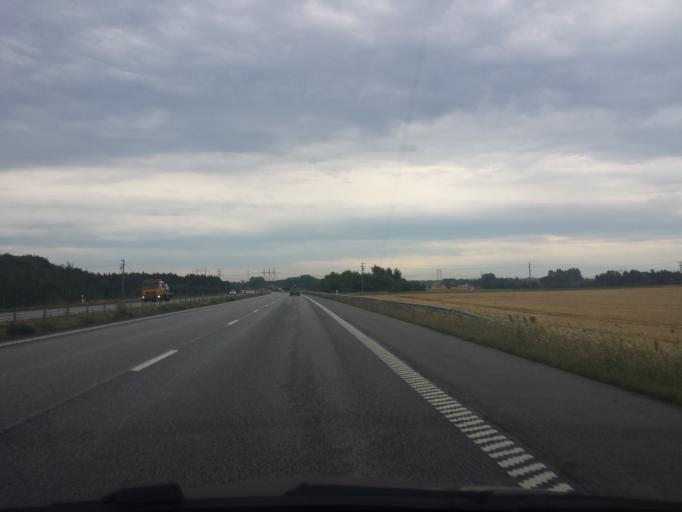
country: SE
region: Skane
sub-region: Svedala Kommun
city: Svedala
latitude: 55.5357
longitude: 13.1747
